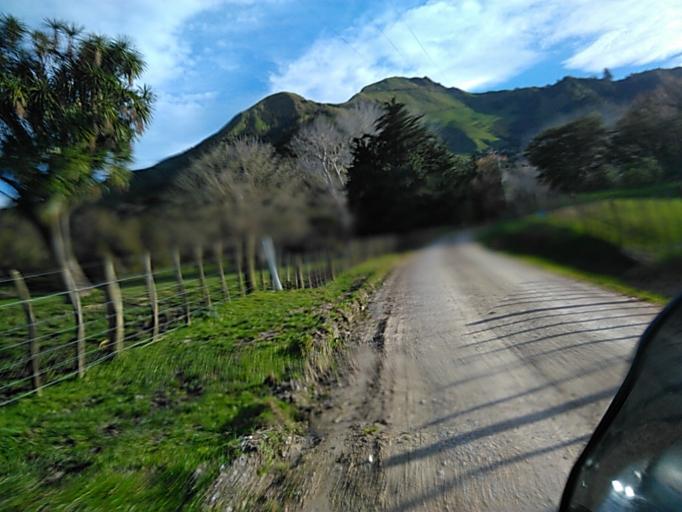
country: NZ
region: Gisborne
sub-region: Gisborne District
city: Gisborne
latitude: -38.5886
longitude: 178.0671
